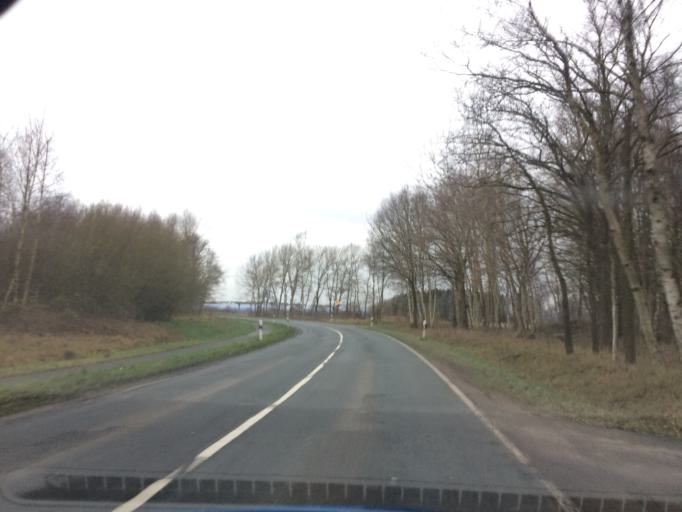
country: DE
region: Lower Saxony
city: Winsen
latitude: 53.3240
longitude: 10.2270
